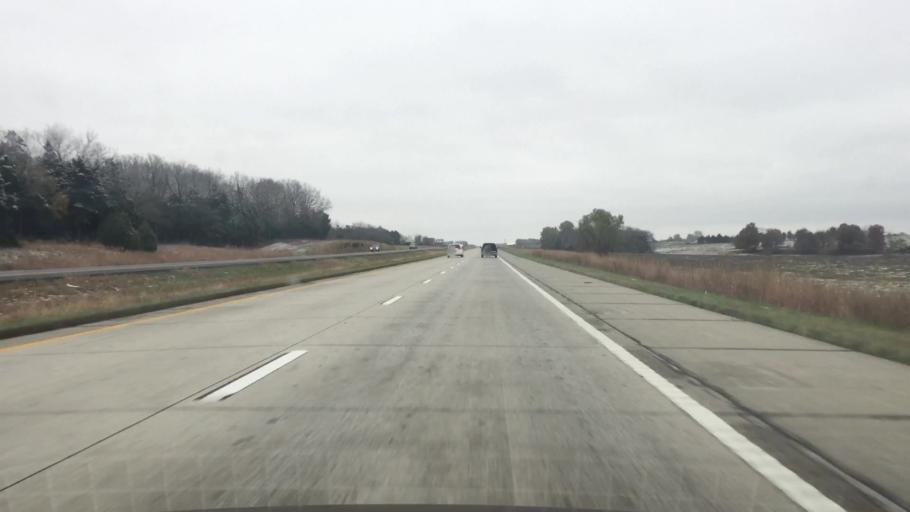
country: US
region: Missouri
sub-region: Saint Clair County
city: Osceola
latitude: 38.0045
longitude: -93.6564
